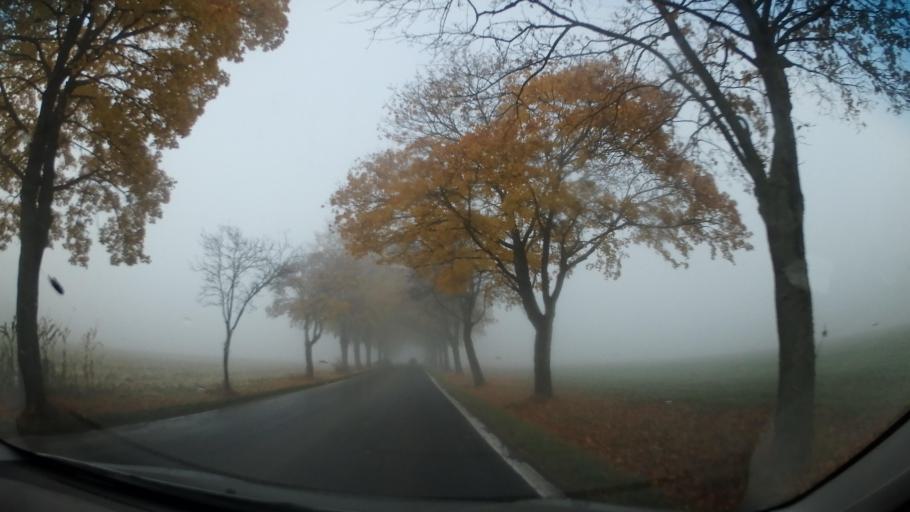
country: CZ
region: Vysocina
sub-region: Okres Zd'ar nad Sazavou
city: Nove Mesto na Morave
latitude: 49.4730
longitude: 16.0772
